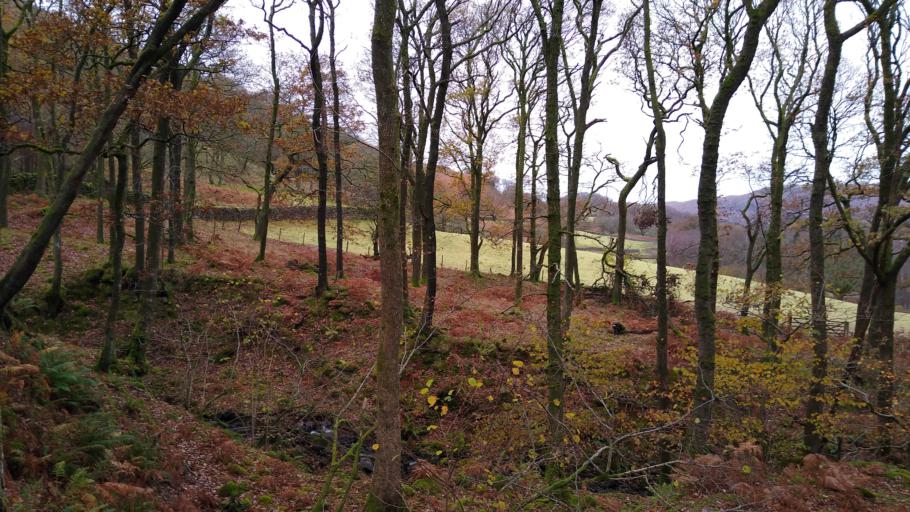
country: GB
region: England
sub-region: Cumbria
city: Millom
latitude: 54.3944
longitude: -3.2285
